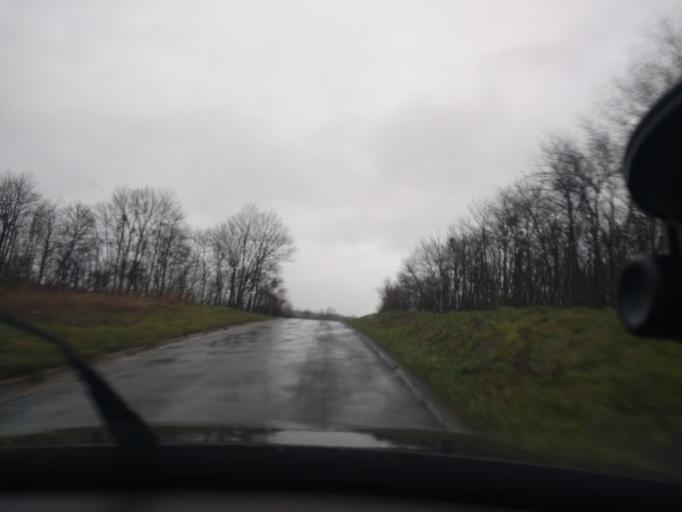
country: DE
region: Rheinland-Pfalz
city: Pellingen
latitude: 49.6934
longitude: 6.6448
